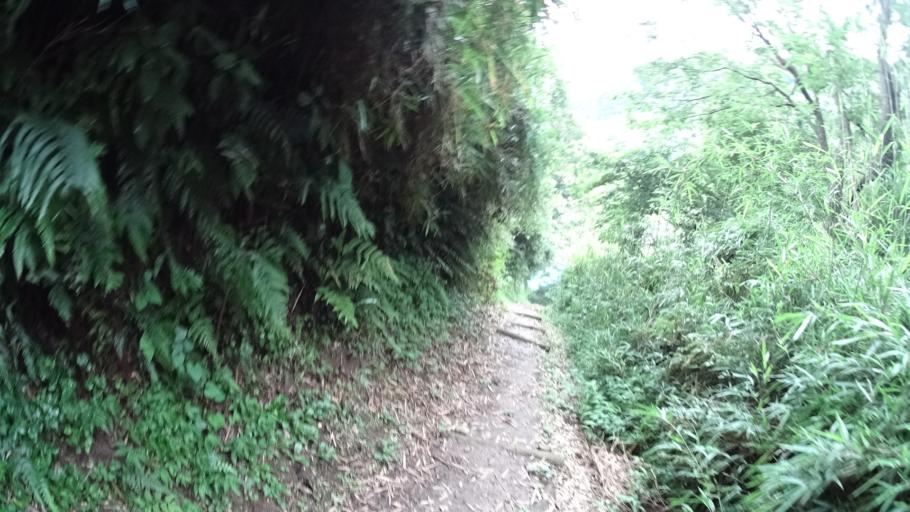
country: JP
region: Kanagawa
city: Yokosuka
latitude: 35.2479
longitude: 139.6559
